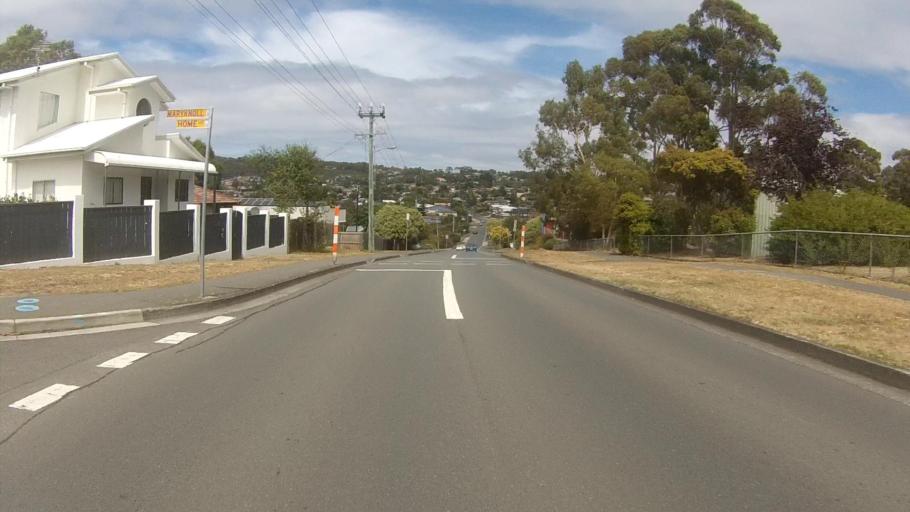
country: AU
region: Tasmania
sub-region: Kingborough
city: Blackmans Bay
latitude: -42.9967
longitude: 147.3230
